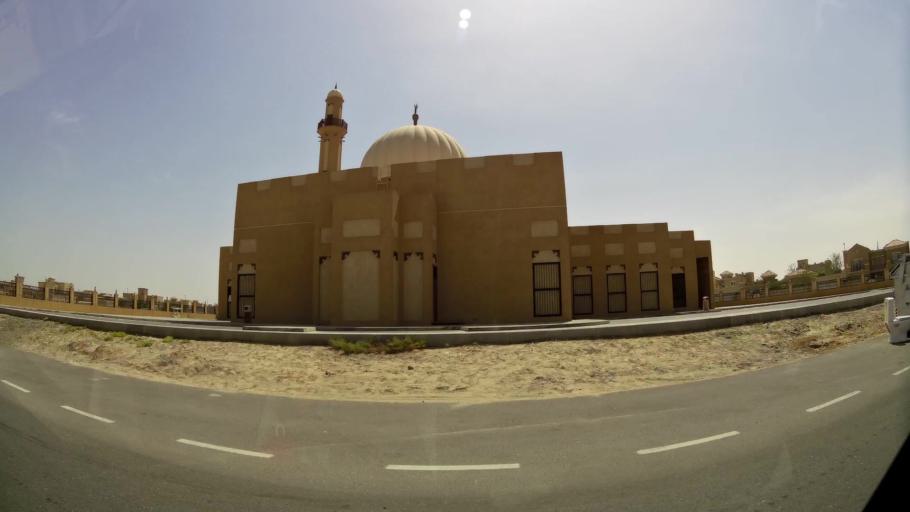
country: AE
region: Ash Shariqah
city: Sharjah
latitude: 25.1774
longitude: 55.4323
